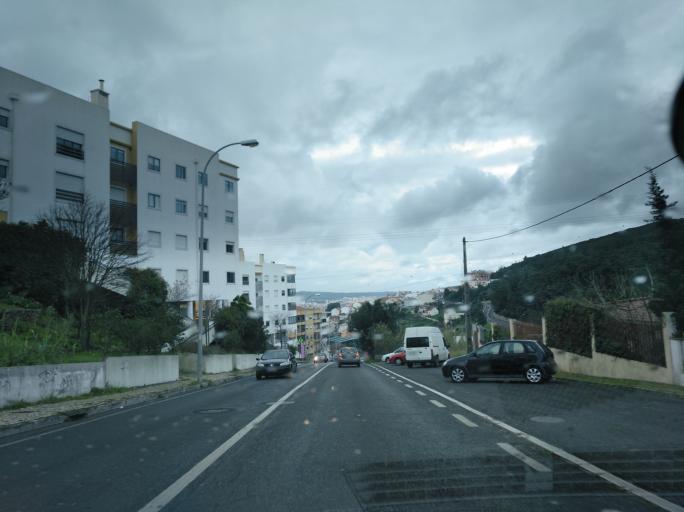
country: PT
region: Lisbon
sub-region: Odivelas
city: Famoes
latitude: 38.7902
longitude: -9.2275
